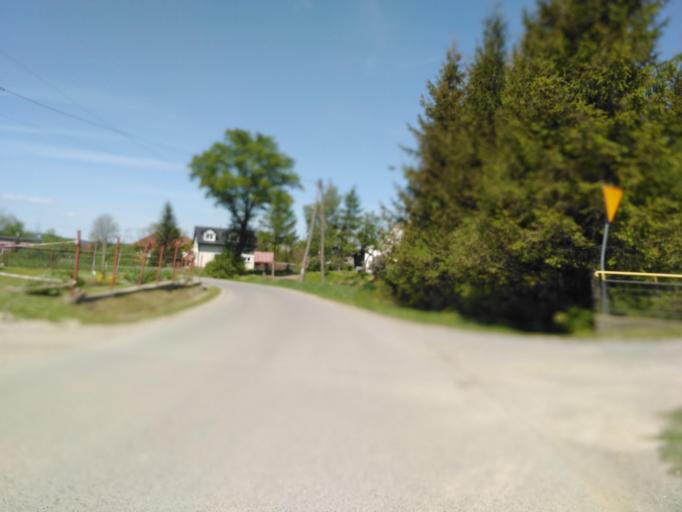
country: PL
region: Subcarpathian Voivodeship
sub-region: Powiat krosnienski
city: Dukla
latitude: 49.5448
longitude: 21.7325
